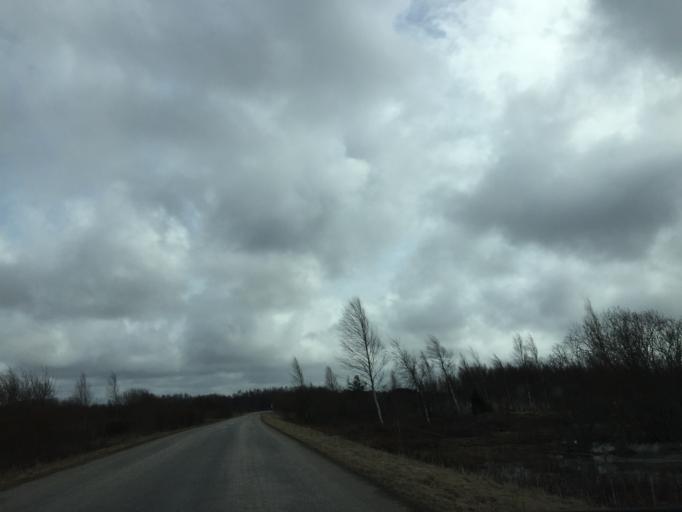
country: EE
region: Laeaene
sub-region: Lihula vald
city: Lihula
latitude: 58.7264
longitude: 23.9118
